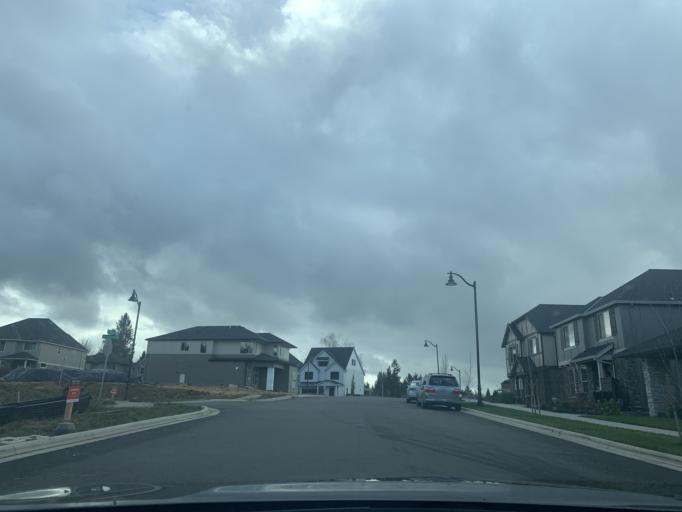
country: US
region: Oregon
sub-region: Washington County
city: Cedar Mill
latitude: 45.5499
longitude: -122.8025
